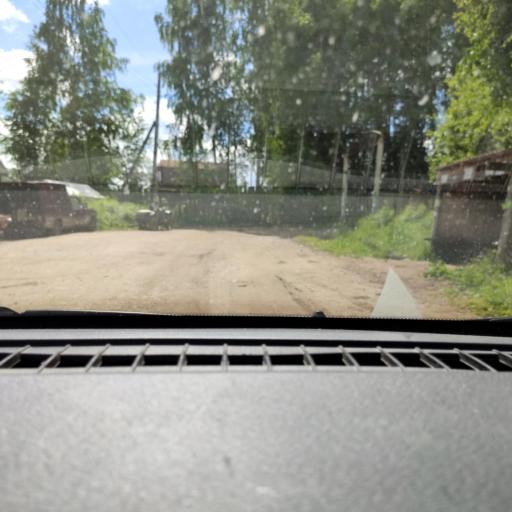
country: RU
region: Perm
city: Overyata
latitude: 58.1405
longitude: 55.8225
